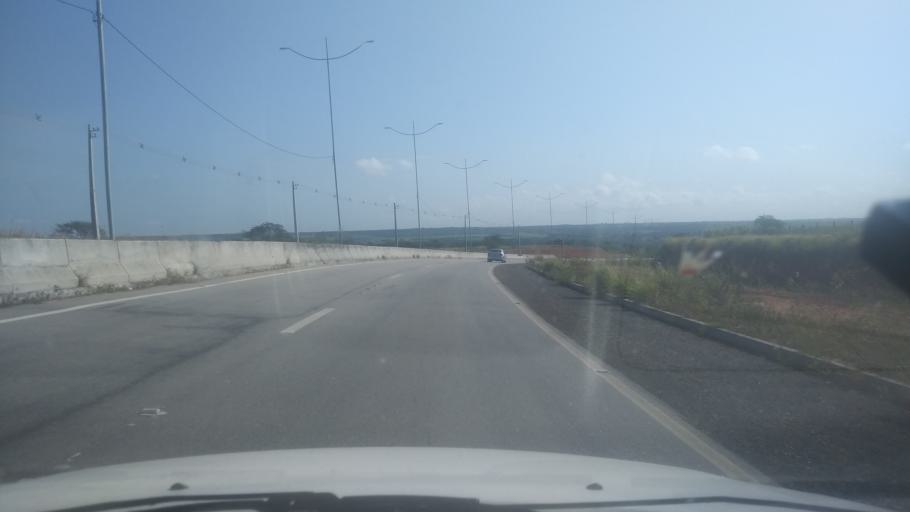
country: BR
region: Rio Grande do Norte
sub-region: Macaiba
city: Macaiba
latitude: -5.8256
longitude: -35.3701
